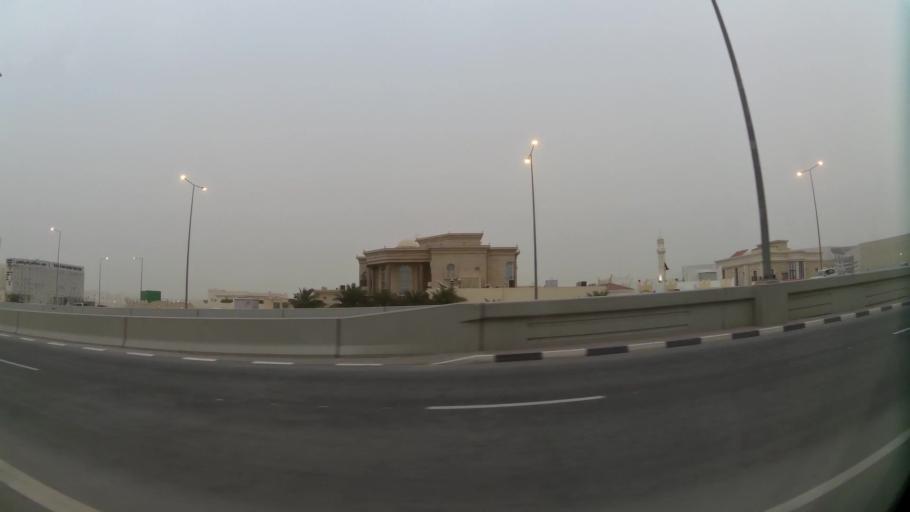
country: QA
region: Baladiyat ad Dawhah
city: Doha
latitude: 25.2333
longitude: 51.5026
